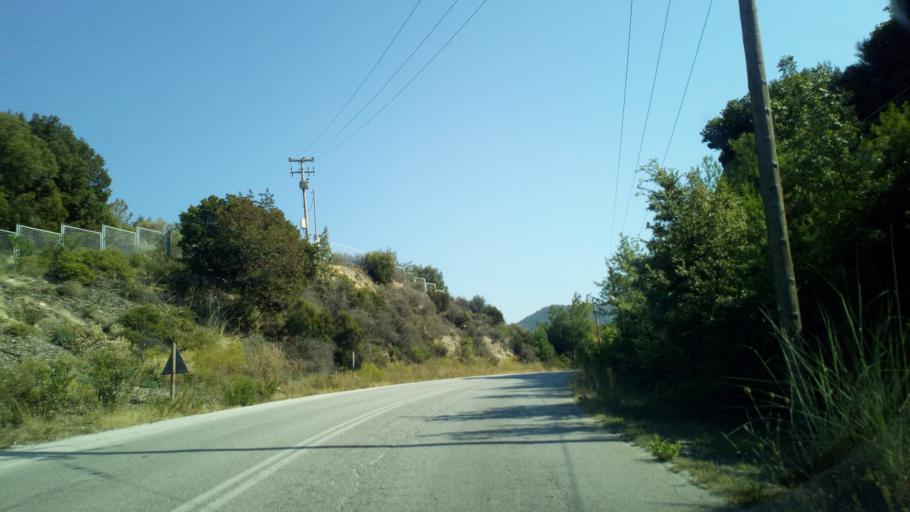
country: GR
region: Central Macedonia
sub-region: Nomos Chalkidikis
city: Stratonion
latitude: 40.5899
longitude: 23.7920
